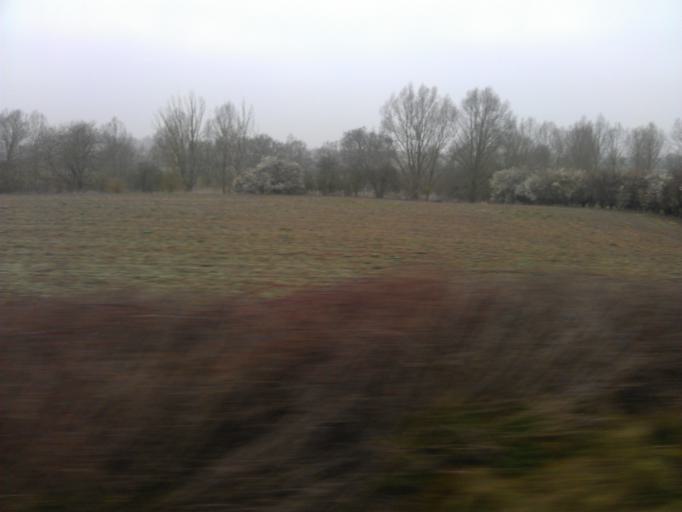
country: GB
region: England
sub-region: Essex
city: Kelvedon
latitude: 51.8446
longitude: 0.7094
